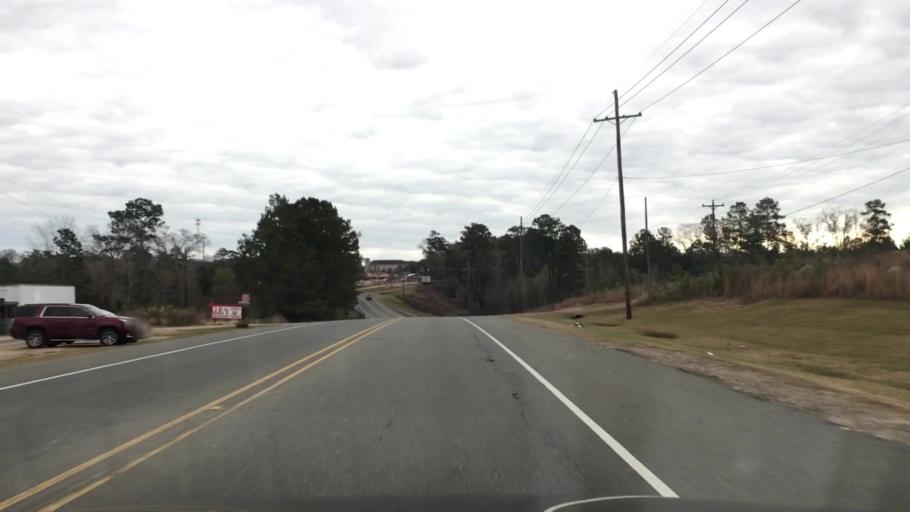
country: US
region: Louisiana
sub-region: Vernon Parish
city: Fort Polk South
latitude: 31.0562
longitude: -93.2516
